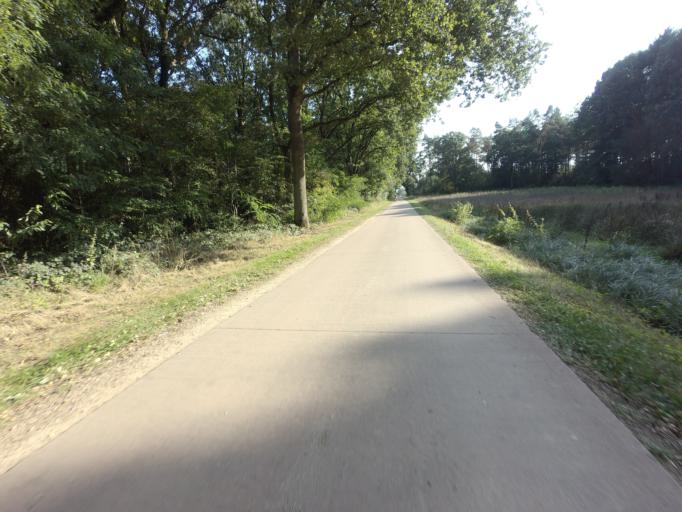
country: NL
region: Limburg
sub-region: Gemeente Roerdalen
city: Sint Odilienberg
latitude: 51.1454
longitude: 5.9833
